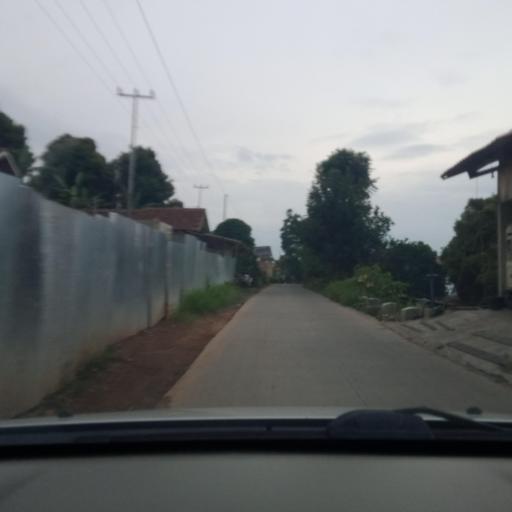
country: ID
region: West Java
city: Lembang
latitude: -6.8212
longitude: 107.5865
